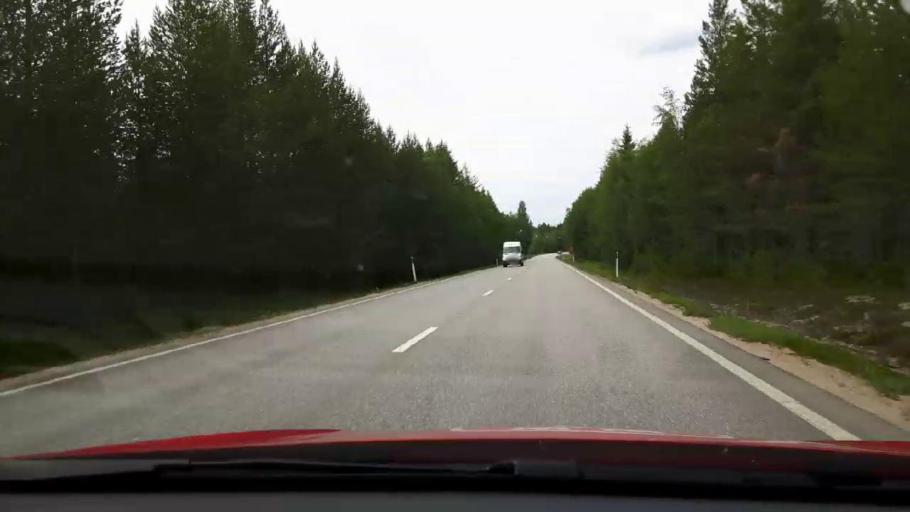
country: SE
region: Jaemtland
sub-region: Harjedalens Kommun
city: Sveg
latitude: 62.0616
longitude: 14.2836
